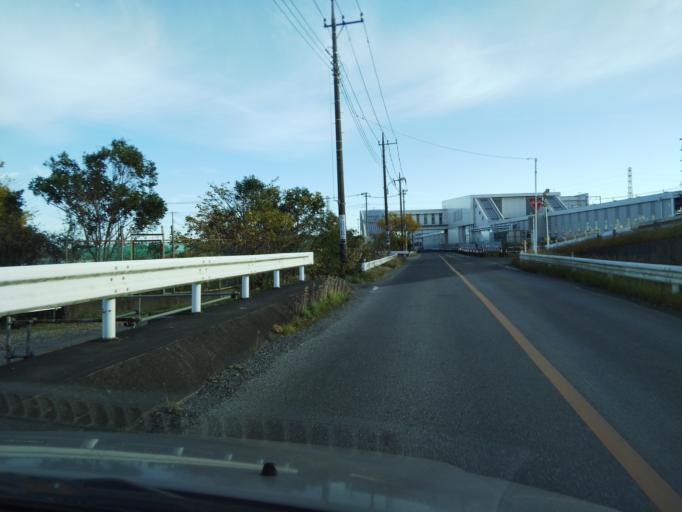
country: JP
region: Saitama
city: Yoshikawa
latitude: 35.8692
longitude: 139.8574
